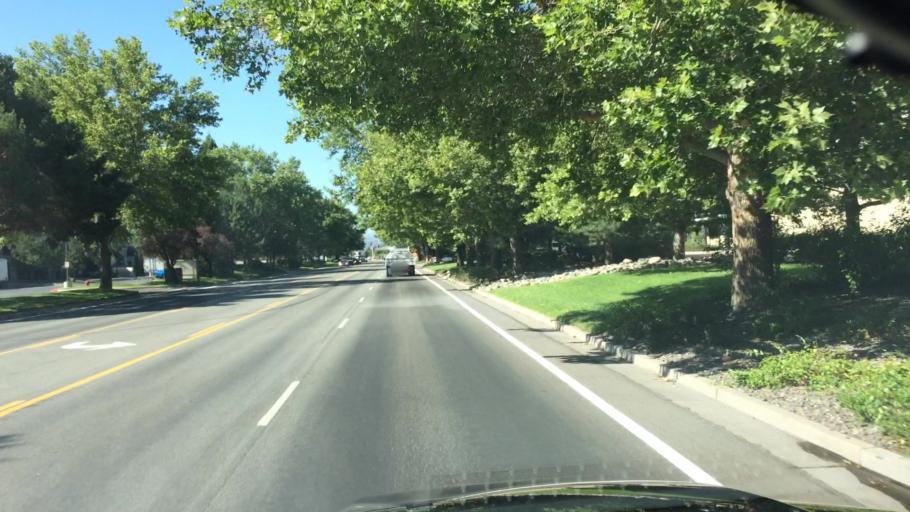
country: US
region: Nevada
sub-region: Washoe County
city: Sparks
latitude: 39.4813
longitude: -119.7630
